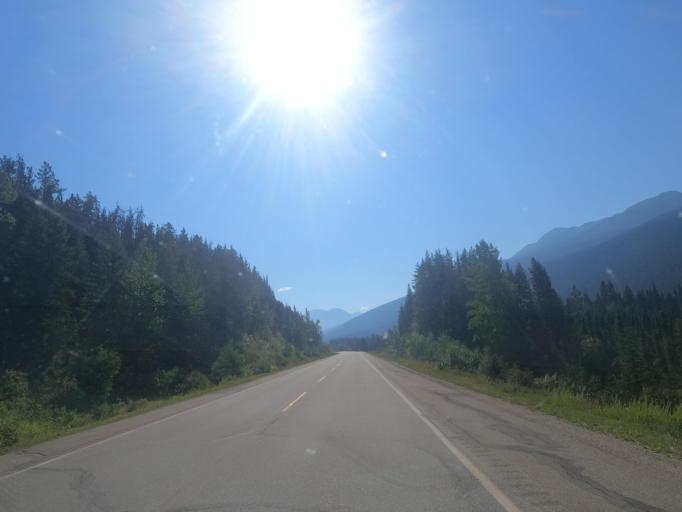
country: CA
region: Alberta
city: Jasper Park Lodge
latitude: 52.8896
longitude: -118.7266
